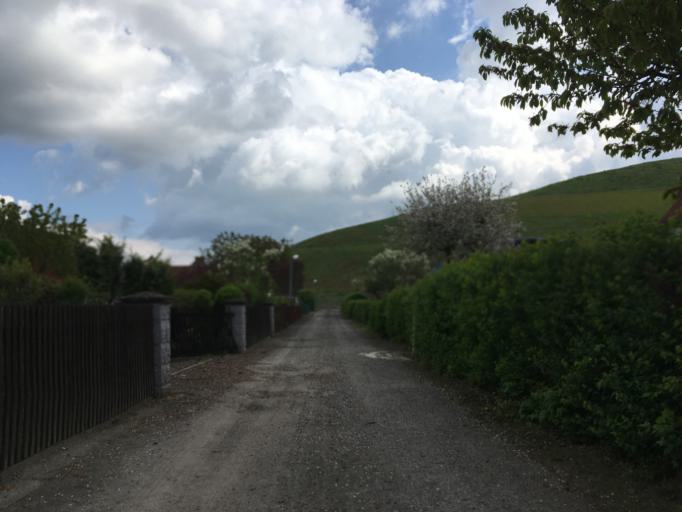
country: DE
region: Berlin
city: Blankenfelde
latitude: 52.6412
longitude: 13.4026
